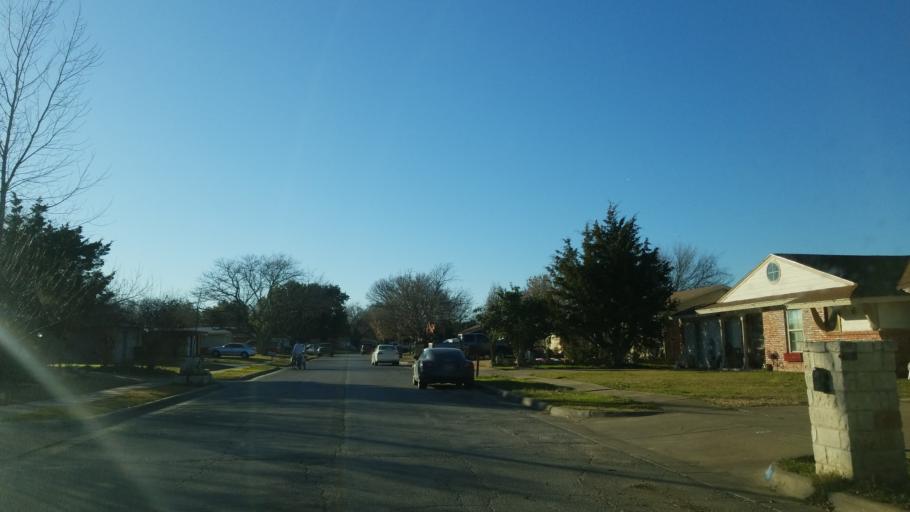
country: US
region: Texas
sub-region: Tarrant County
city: Arlington
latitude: 32.7290
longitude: -97.0640
